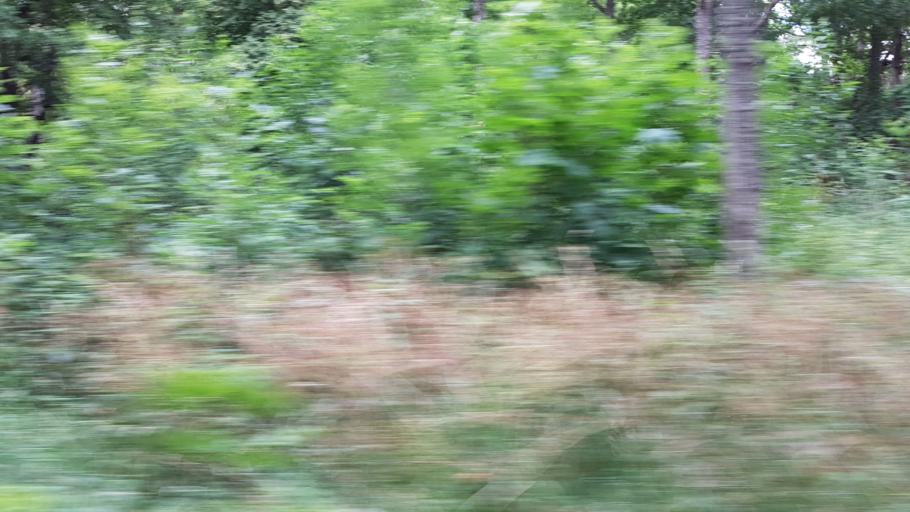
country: SE
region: OEstergoetland
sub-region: Valdemarsviks Kommun
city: Gusum
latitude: 58.4370
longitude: 16.5986
